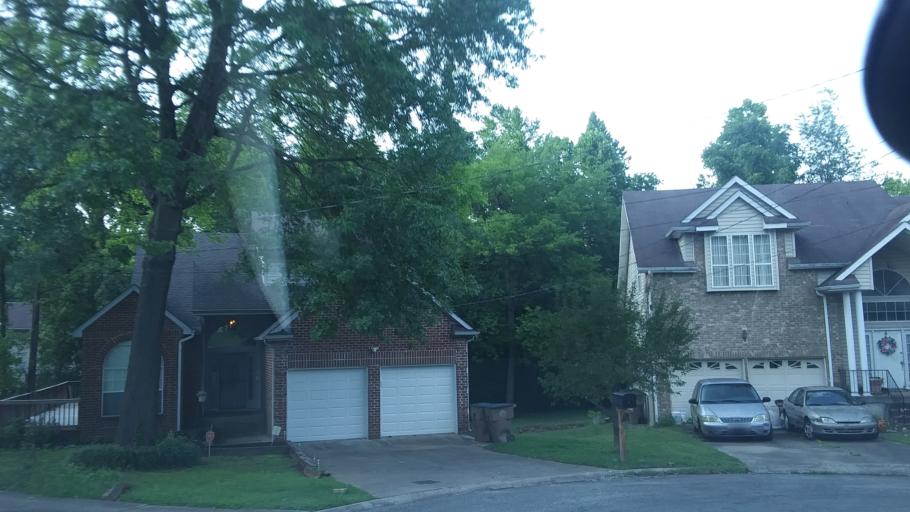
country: US
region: Tennessee
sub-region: Rutherford County
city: La Vergne
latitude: 36.0784
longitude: -86.6667
